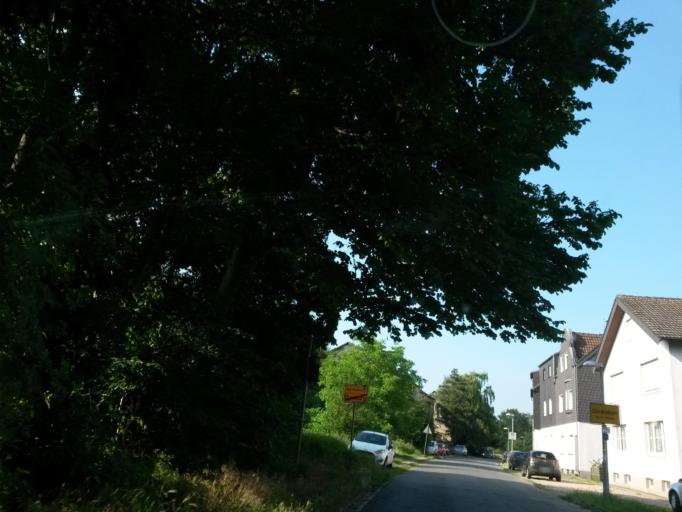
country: DE
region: North Rhine-Westphalia
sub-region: Regierungsbezirk Dusseldorf
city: Dinslaken
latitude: 51.5484
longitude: 6.7271
